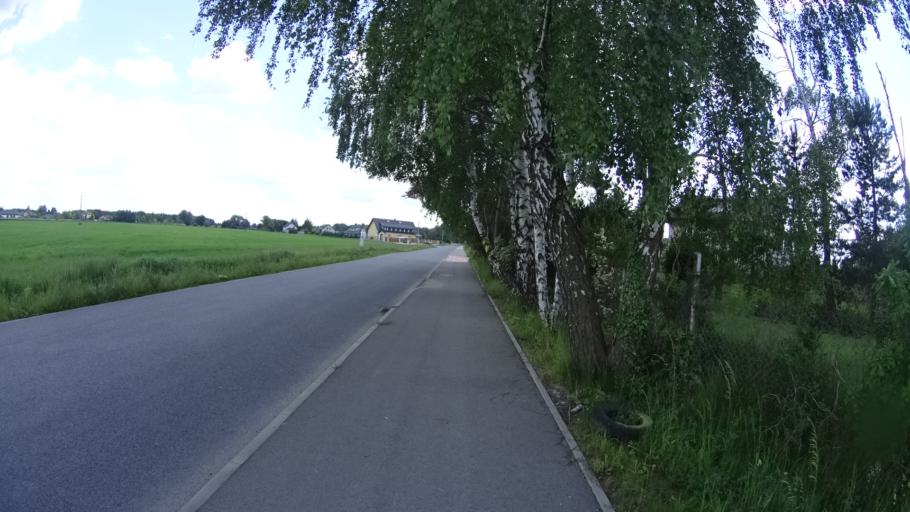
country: PL
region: Masovian Voivodeship
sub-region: Powiat pruszkowski
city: Nadarzyn
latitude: 52.0841
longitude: 20.8163
